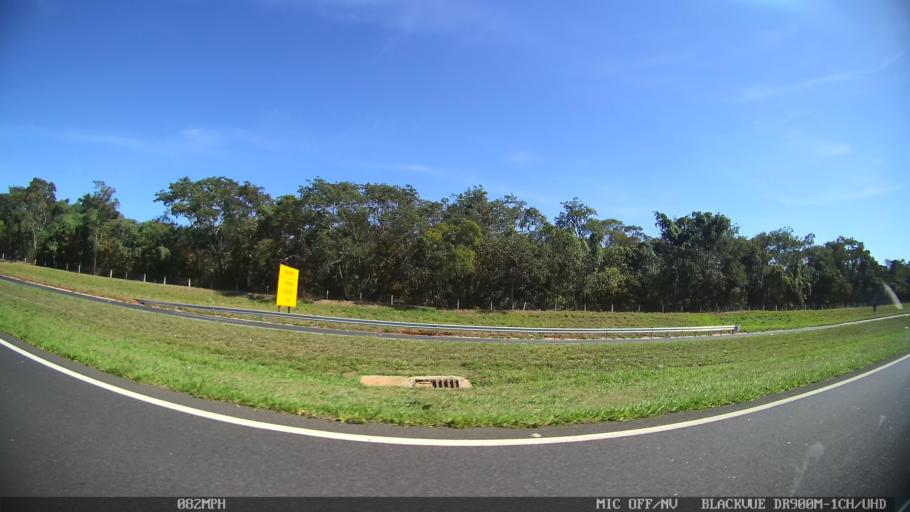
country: BR
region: Sao Paulo
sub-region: Sao Simao
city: Sao Simao
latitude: -21.6152
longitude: -47.6161
